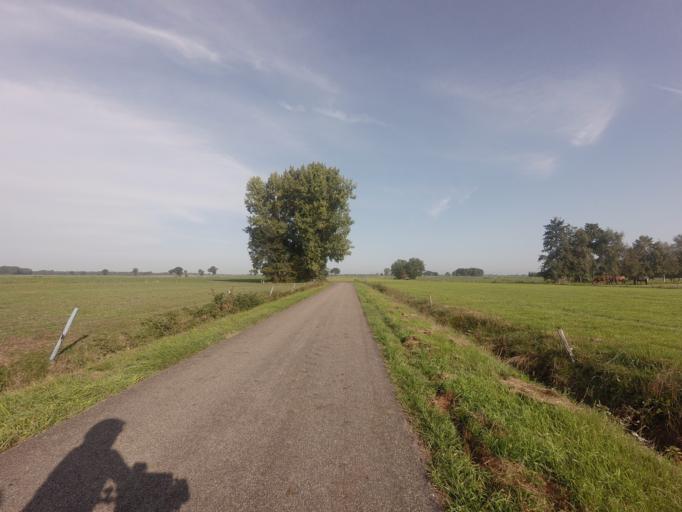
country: NL
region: Groningen
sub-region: Gemeente Leek
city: Leek
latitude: 53.1590
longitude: 6.4328
